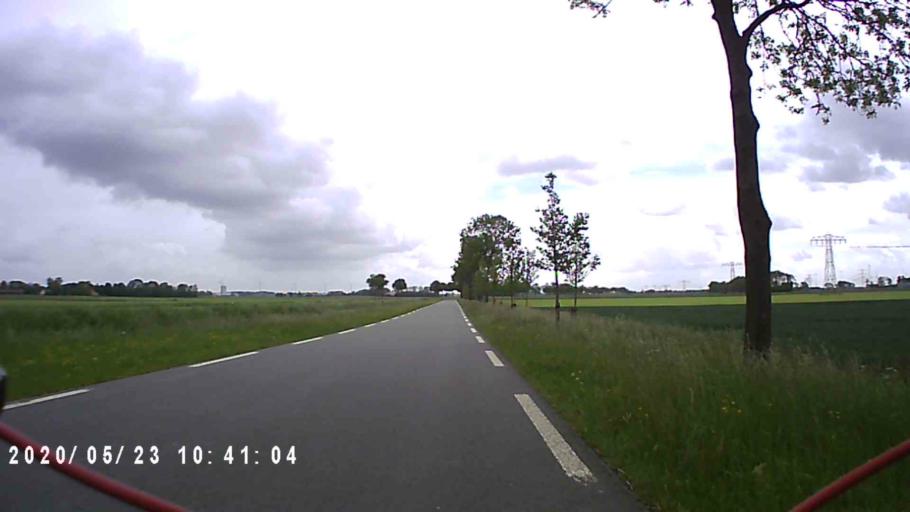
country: NL
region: Groningen
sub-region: Gemeente Delfzijl
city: Delfzijl
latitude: 53.3023
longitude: 6.8967
